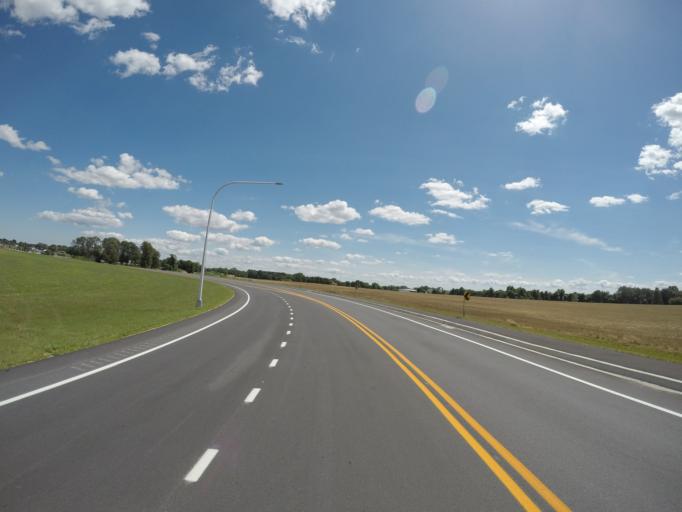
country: US
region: Delaware
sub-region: Sussex County
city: Milford
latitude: 38.9264
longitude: -75.4179
